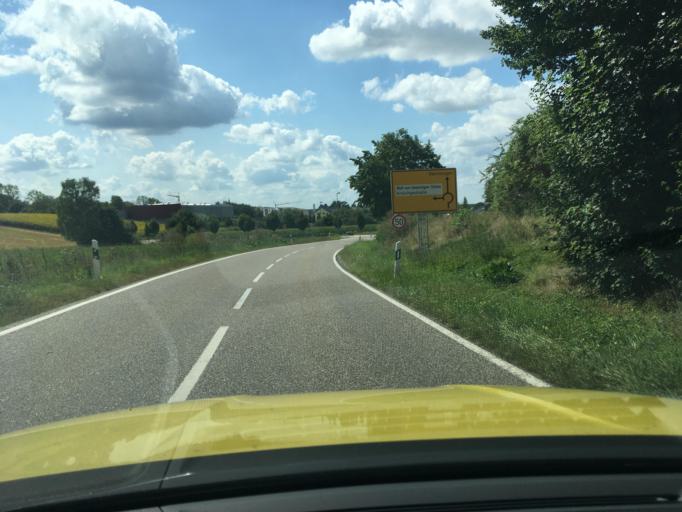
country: DE
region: Baden-Wuerttemberg
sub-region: Regierungsbezirk Stuttgart
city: Gemmingen
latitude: 49.1597
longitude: 8.9926
